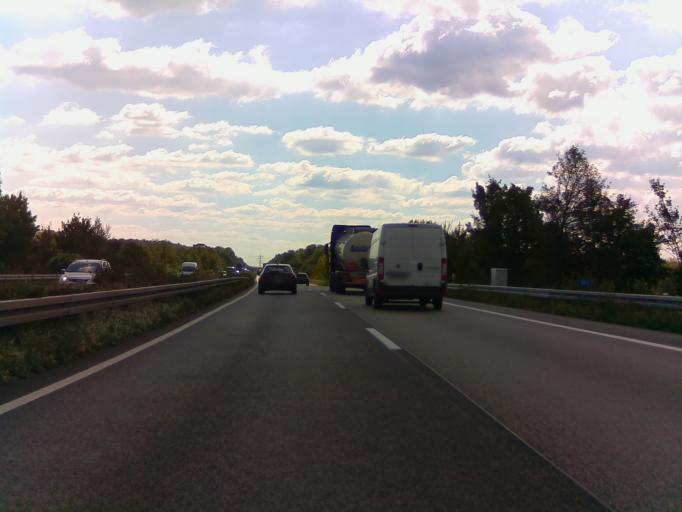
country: DE
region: Hesse
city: Gernsheim
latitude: 49.7644
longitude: 8.5439
